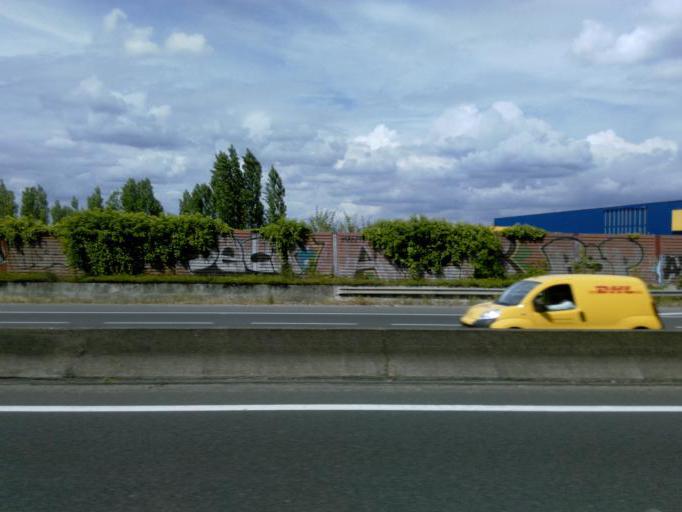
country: FR
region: Ile-de-France
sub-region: Departement du Val-d'Oise
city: Montigny-les-Cormeilles
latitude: 48.9858
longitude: 2.2127
